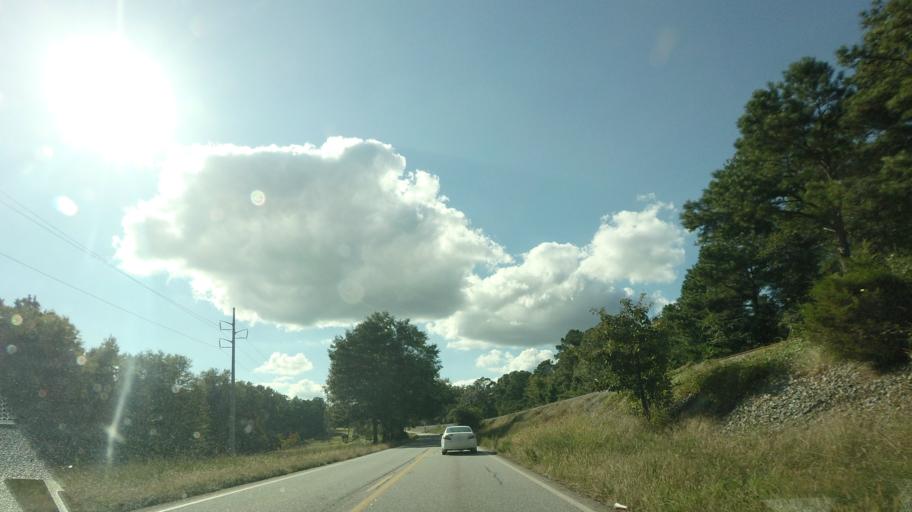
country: US
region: Georgia
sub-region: Monroe County
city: Forsyth
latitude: 33.0533
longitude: -84.0401
